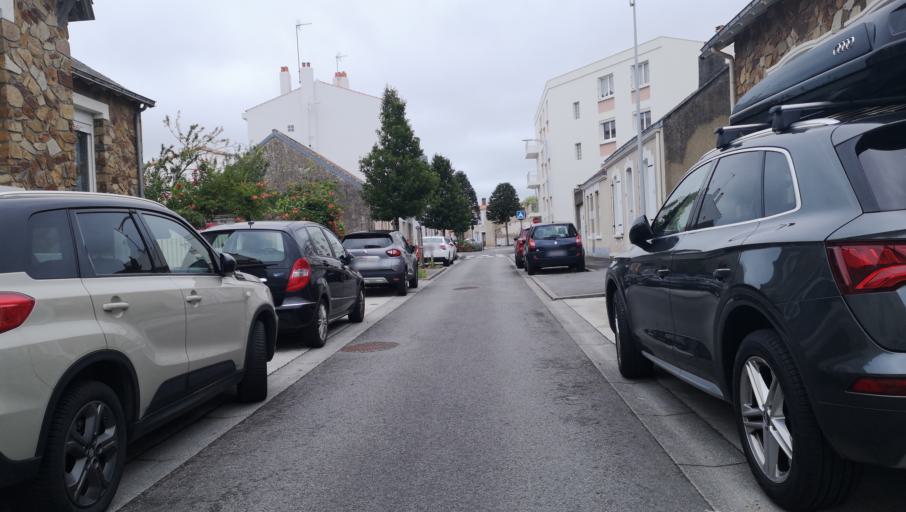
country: FR
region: Pays de la Loire
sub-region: Departement de la Vendee
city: Les Sables-d'Olonne
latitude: 46.5025
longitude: -1.7787
